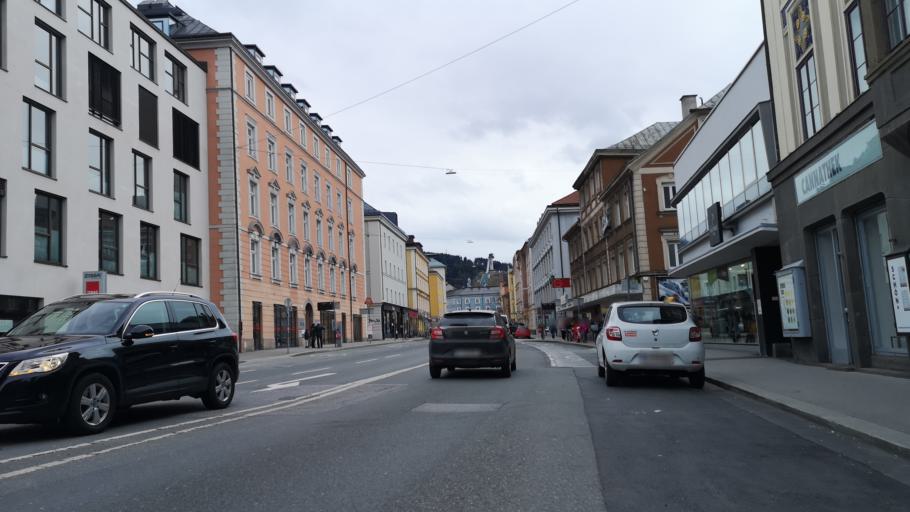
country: AT
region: Tyrol
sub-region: Innsbruck Stadt
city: Innsbruck
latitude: 47.2625
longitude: 11.3948
